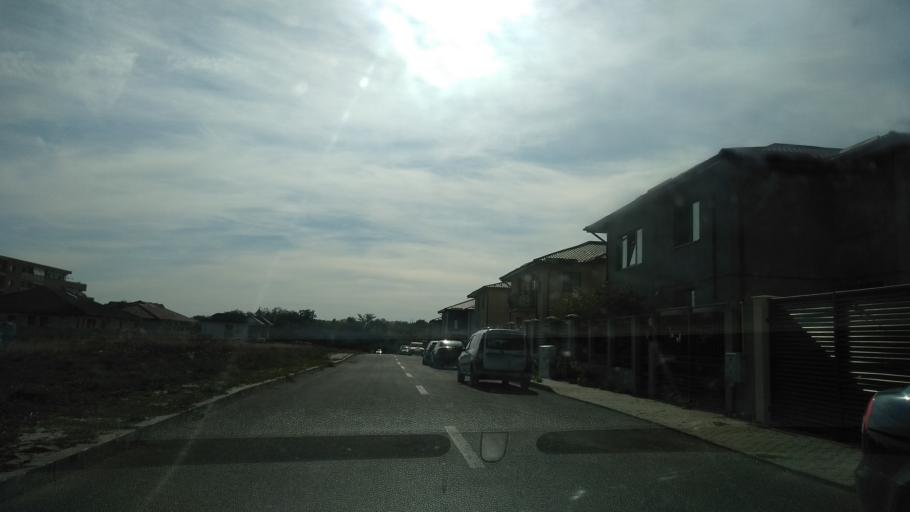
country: RO
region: Ilfov
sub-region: Comuna Chitila
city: Chitila
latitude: 44.5140
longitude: 25.9870
